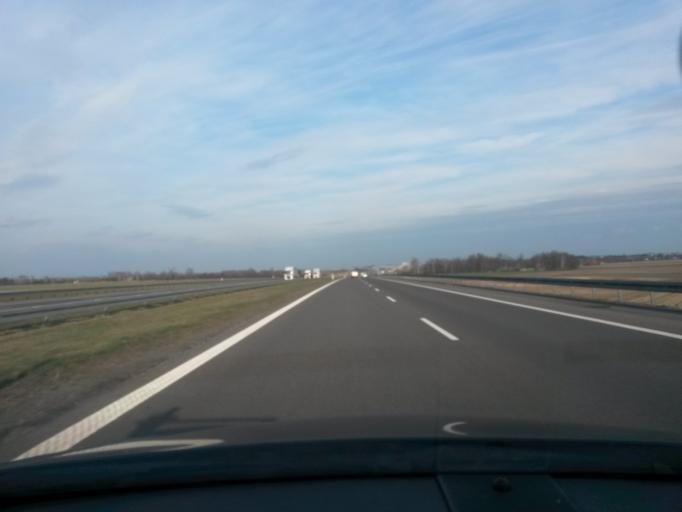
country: PL
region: Lodz Voivodeship
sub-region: Powiat zgierski
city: Strykow
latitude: 51.8980
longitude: 19.5213
